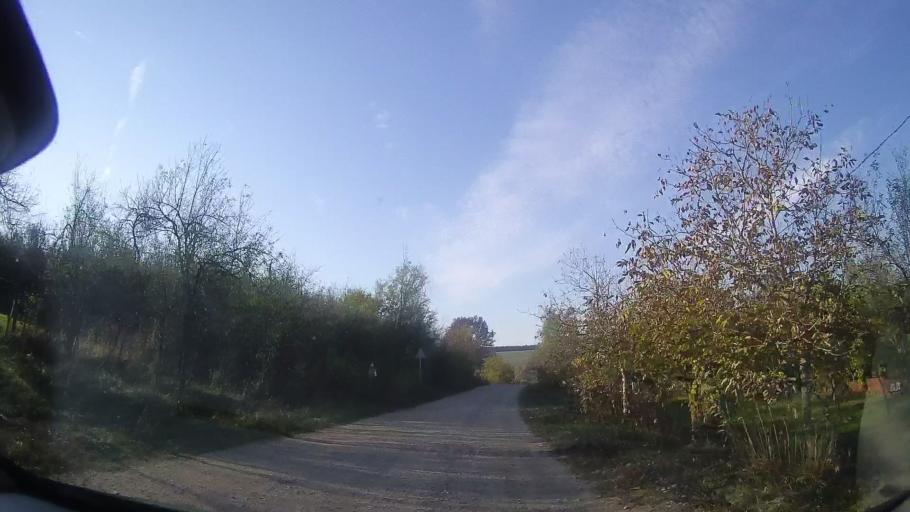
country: RO
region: Timis
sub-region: Comuna Bogda
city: Bogda
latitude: 45.9567
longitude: 21.6150
